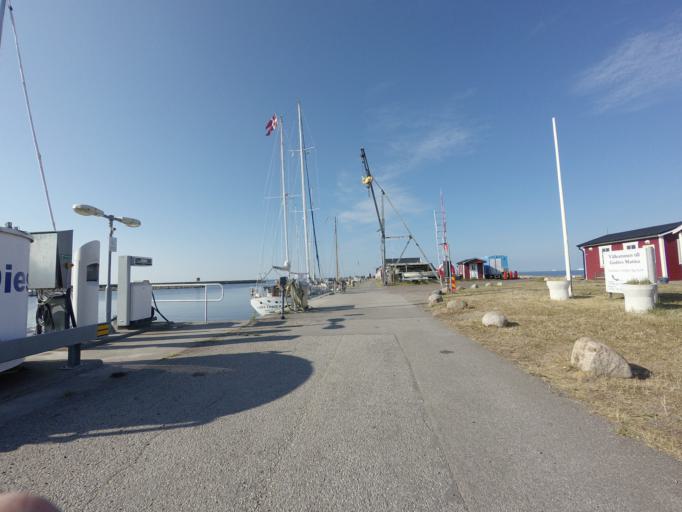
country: SE
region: Skane
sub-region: Trelleborgs Kommun
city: Trelleborg
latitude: 55.3560
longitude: 13.2284
